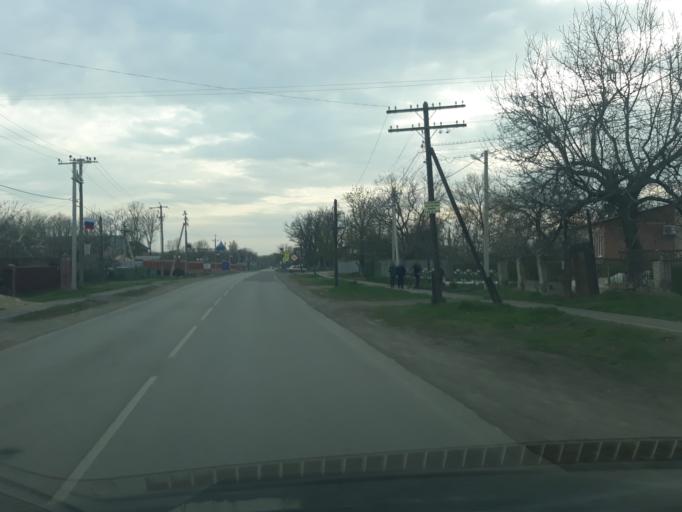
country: RU
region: Rostov
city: Novobessergenovka
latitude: 47.1693
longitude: 38.7428
